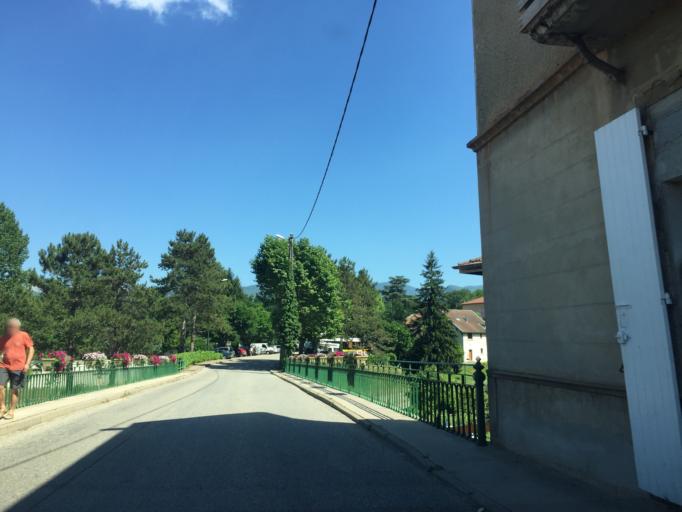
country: FR
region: Rhone-Alpes
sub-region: Departement de l'Isere
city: Saint-Hilaire-du-Rosier
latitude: 45.0604
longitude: 5.2481
